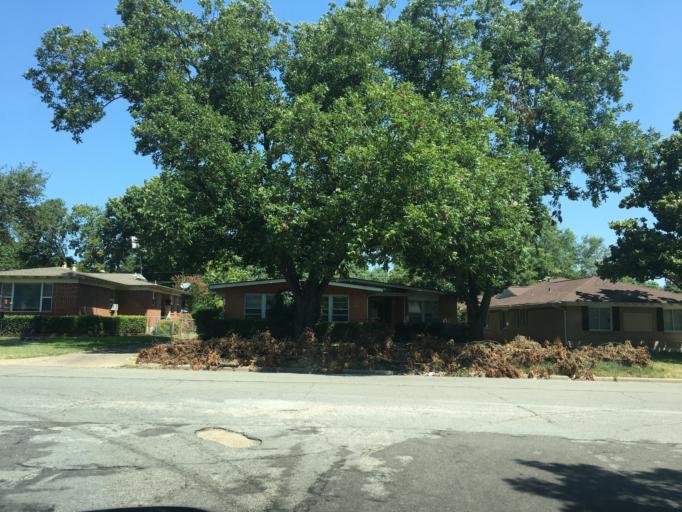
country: US
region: Texas
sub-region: Dallas County
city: Highland Park
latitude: 32.8384
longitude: -96.7500
